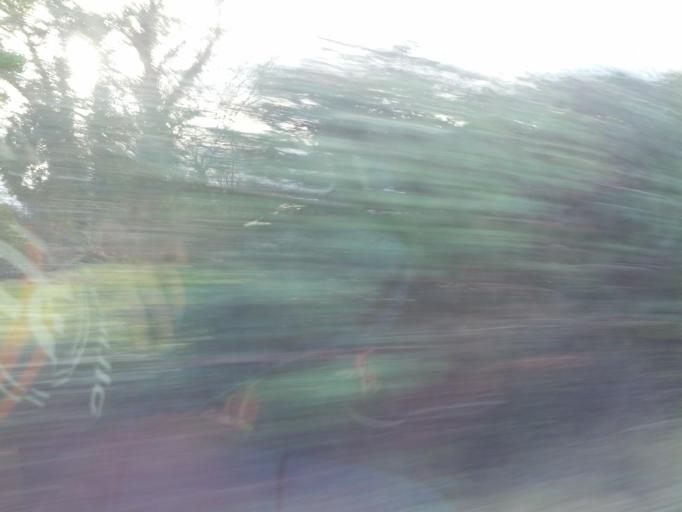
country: IE
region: Connaught
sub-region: County Galway
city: Athenry
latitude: 53.3893
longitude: -8.6078
